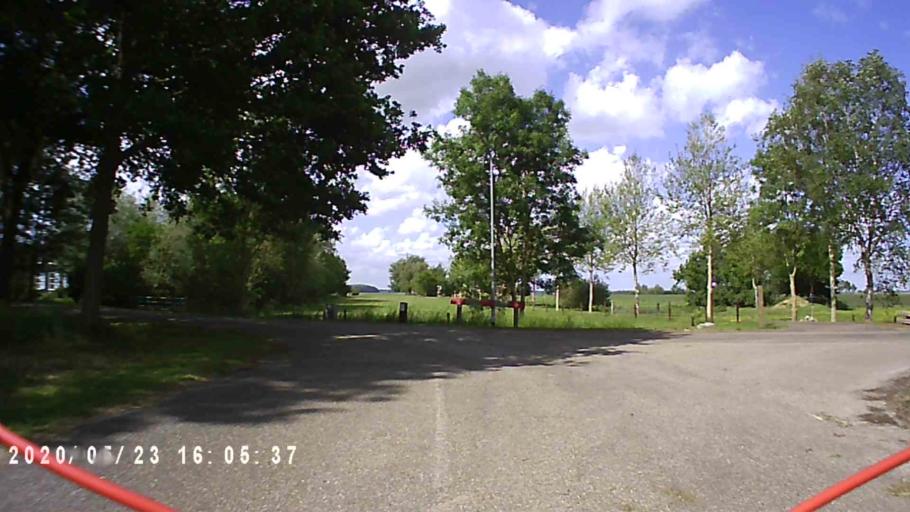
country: NL
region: Groningen
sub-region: Gemeente Appingedam
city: Appingedam
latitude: 53.2460
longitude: 6.8937
